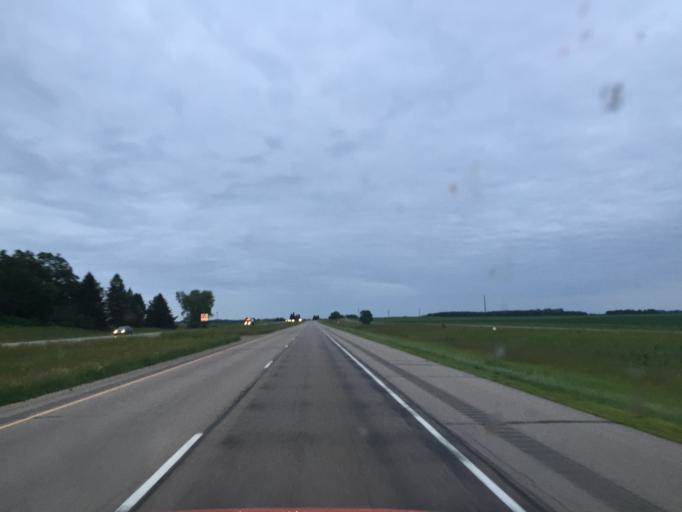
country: US
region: Minnesota
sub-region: Mower County
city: Austin
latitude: 43.6592
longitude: -93.0795
